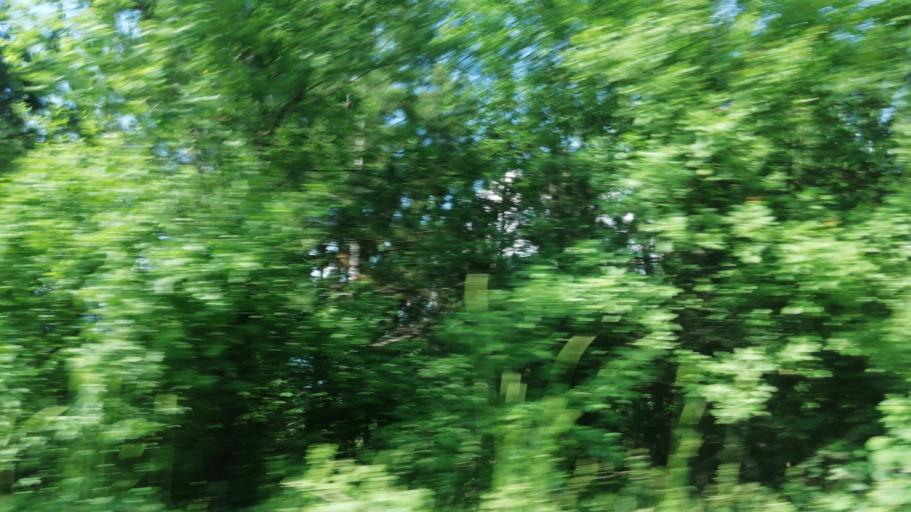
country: TR
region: Karabuk
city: Karabuk
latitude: 41.1249
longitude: 32.5878
